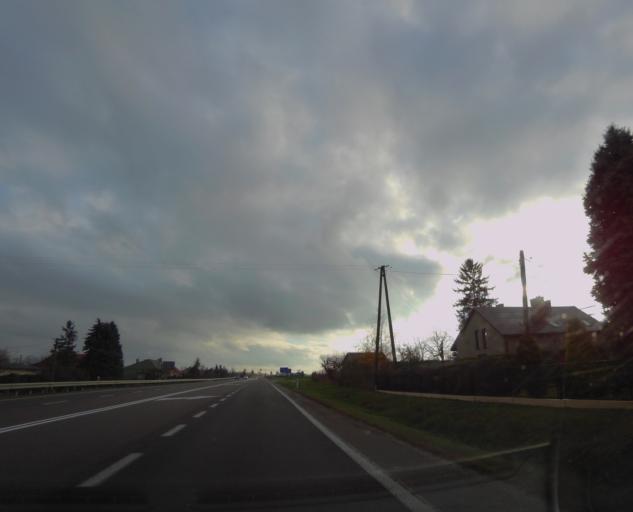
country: PL
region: Subcarpathian Voivodeship
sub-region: Powiat przemyski
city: Orly
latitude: 49.8970
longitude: 22.8164
